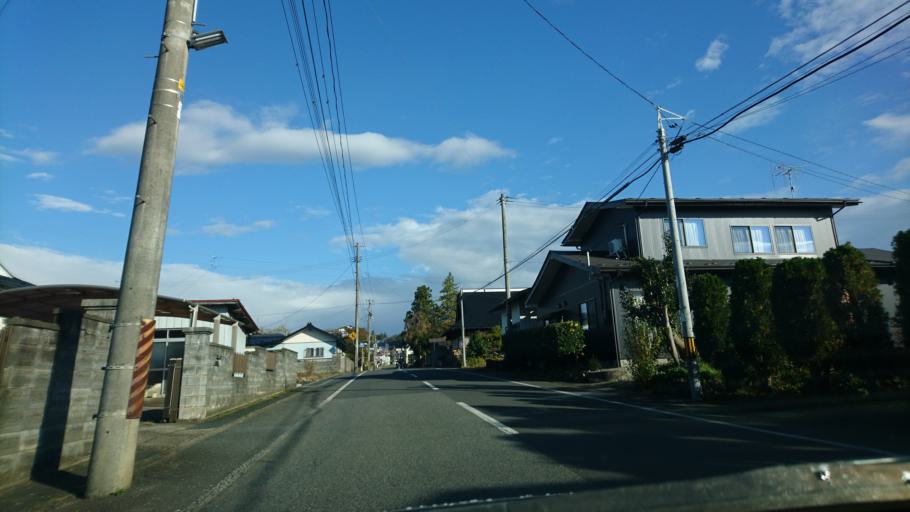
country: JP
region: Iwate
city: Ichinoseki
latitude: 39.0118
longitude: 141.1099
